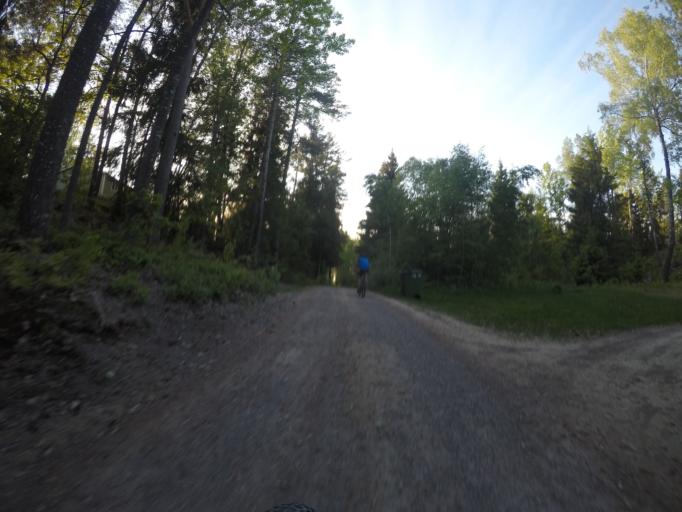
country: SE
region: Soedermanland
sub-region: Eskilstuna Kommun
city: Skogstorp
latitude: 59.3331
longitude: 16.4903
